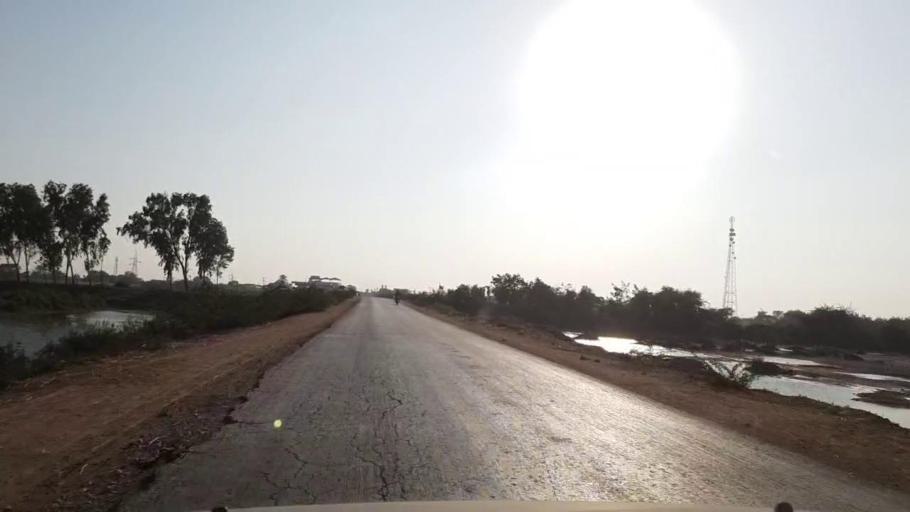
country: PK
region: Sindh
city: Mirpur Batoro
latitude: 24.7397
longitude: 68.2586
